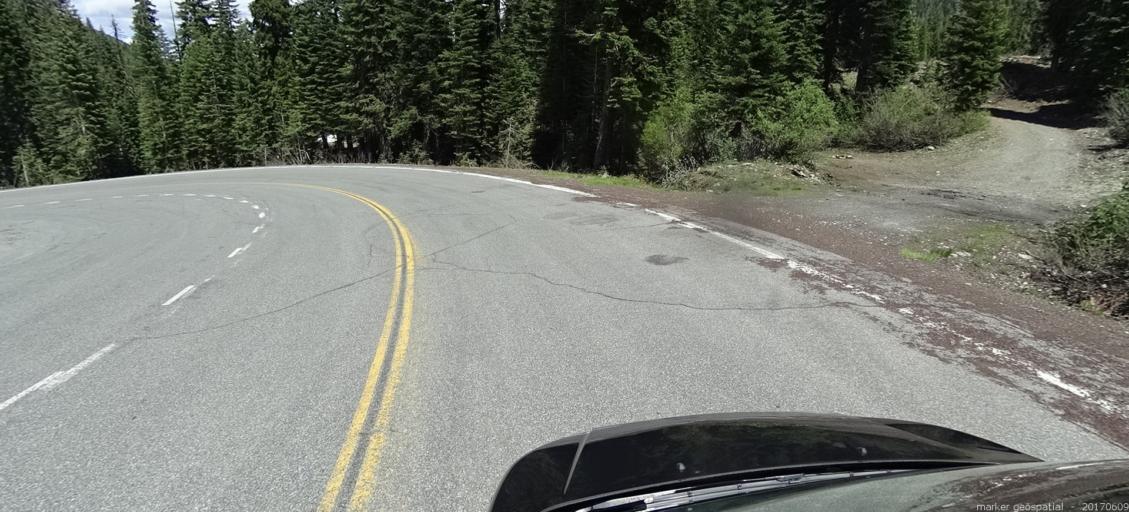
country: US
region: California
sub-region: Siskiyou County
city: Yreka
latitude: 41.4003
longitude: -122.9866
